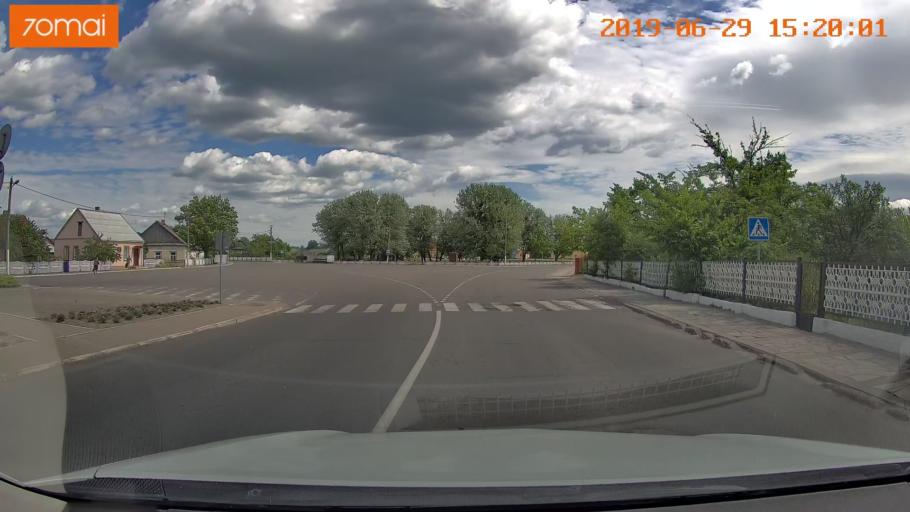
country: BY
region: Brest
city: Mikashevichy
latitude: 52.2166
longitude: 27.4709
